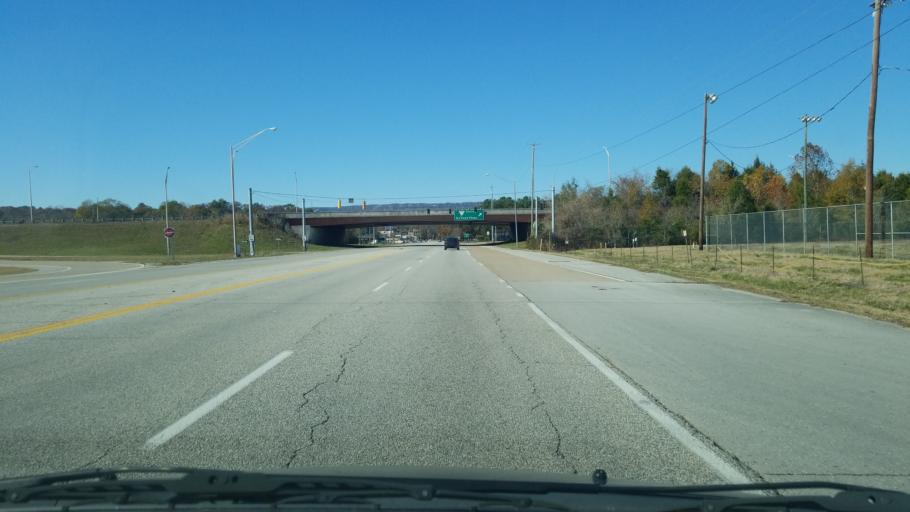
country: US
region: Tennessee
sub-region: Hamilton County
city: Red Bank
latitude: 35.1113
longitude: -85.2494
